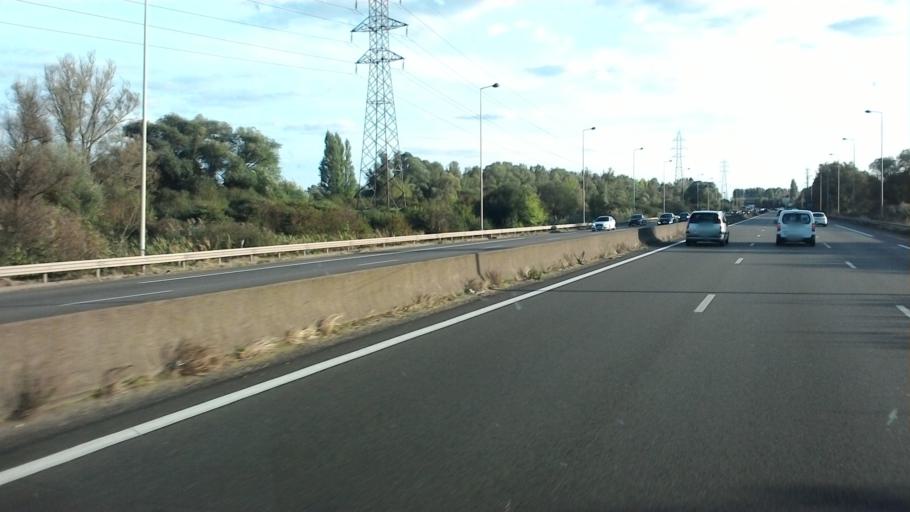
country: FR
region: Lorraine
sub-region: Departement de la Moselle
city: Mondelange
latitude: 49.2569
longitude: 6.1768
